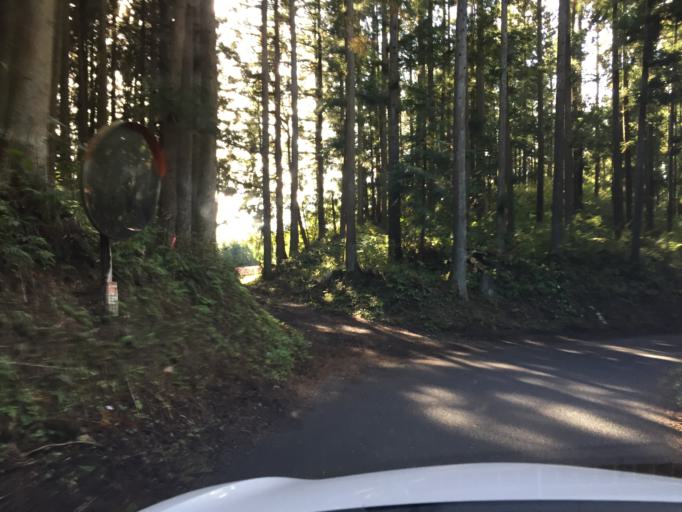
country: JP
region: Fukushima
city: Ishikawa
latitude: 37.1688
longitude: 140.4806
